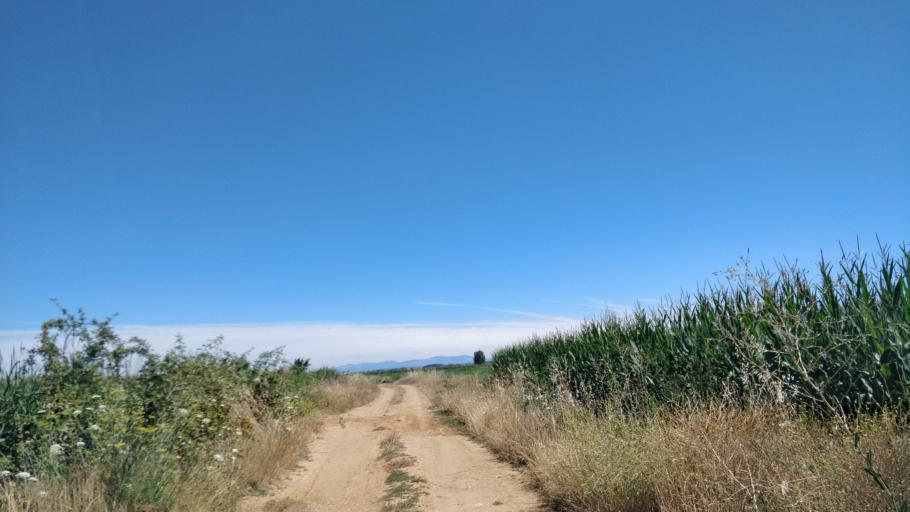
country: ES
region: Castille and Leon
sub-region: Provincia de Leon
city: Bustillo del Paramo
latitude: 42.4442
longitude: -5.8151
